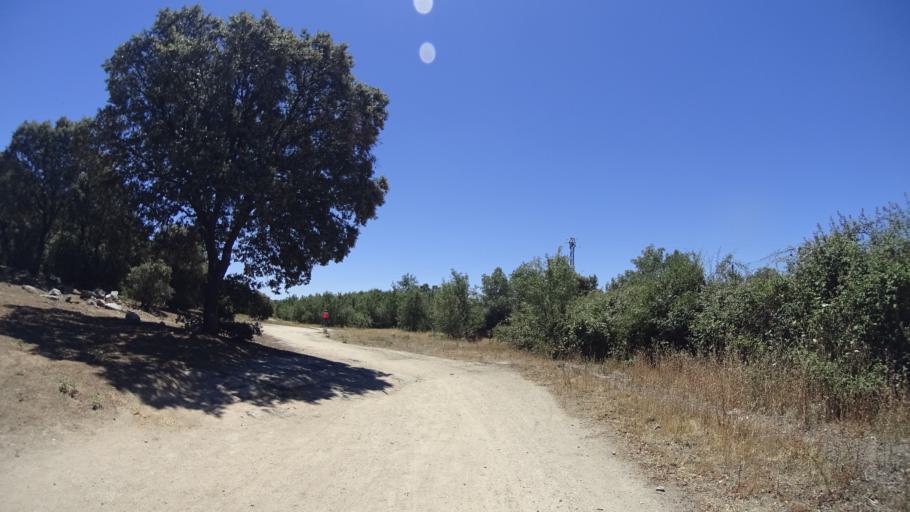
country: ES
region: Madrid
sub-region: Provincia de Madrid
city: Alpedrete
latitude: 40.6601
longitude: -4.0117
